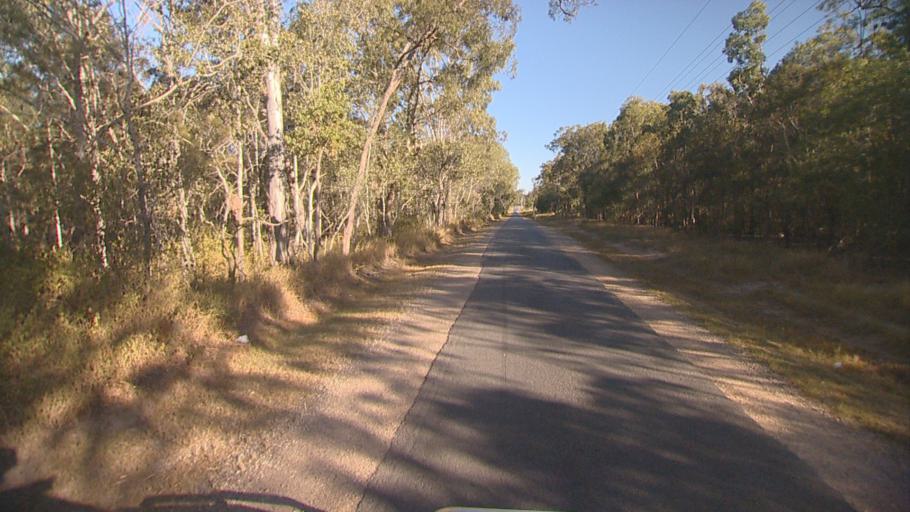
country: AU
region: Queensland
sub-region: Logan
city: North Maclean
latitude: -27.7861
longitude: 153.0389
